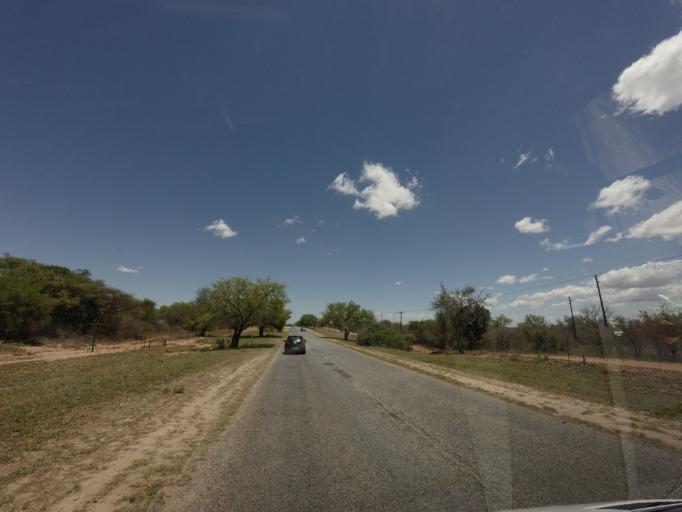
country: ZA
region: Limpopo
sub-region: Mopani District Municipality
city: Hoedspruit
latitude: -24.3938
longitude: 30.7575
